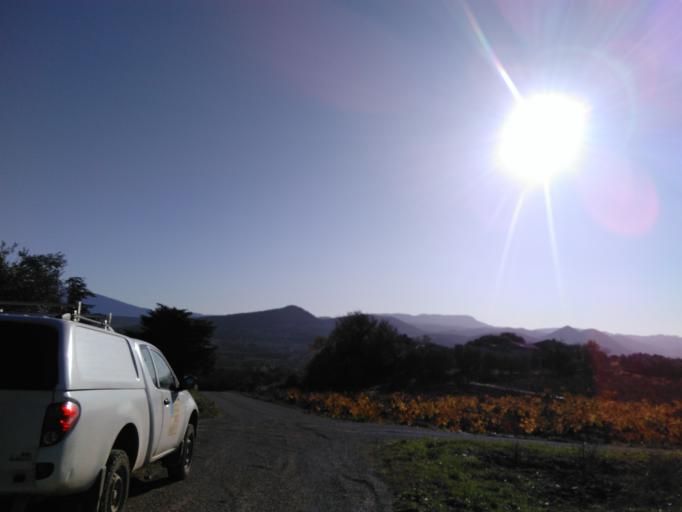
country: FR
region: Provence-Alpes-Cote d'Azur
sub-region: Departement du Vaucluse
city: Sablet
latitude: 44.2547
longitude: 5.0097
